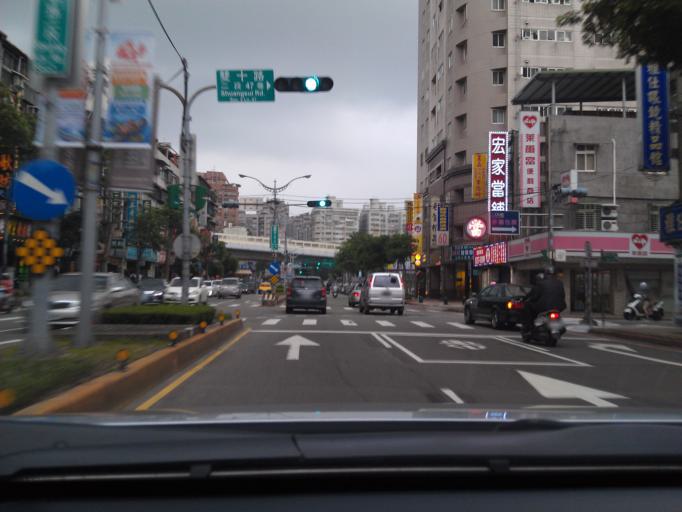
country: TW
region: Taipei
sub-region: Taipei
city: Banqiao
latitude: 25.0265
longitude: 121.4765
